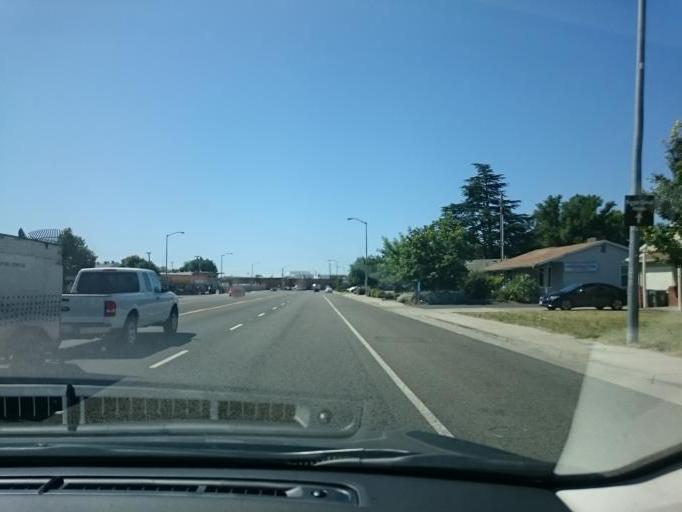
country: US
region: California
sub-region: Yolo County
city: West Sacramento
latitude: 38.5736
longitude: -121.5240
